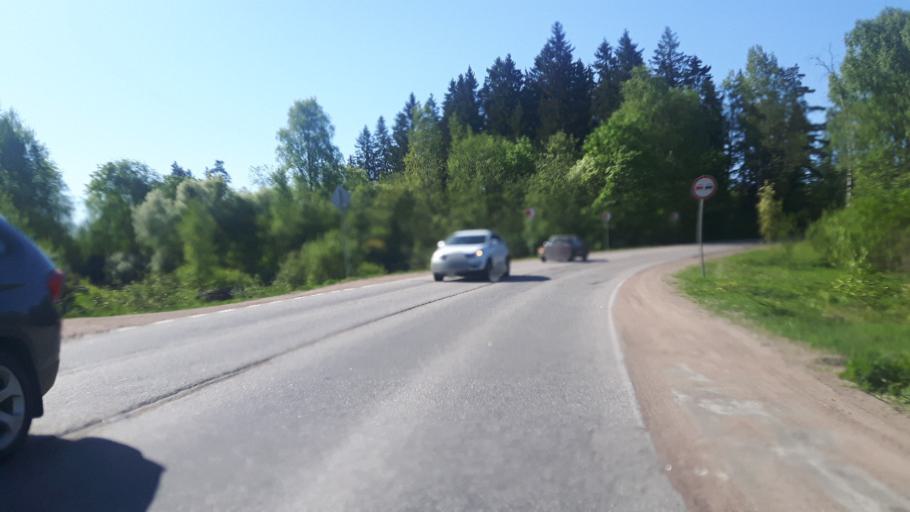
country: RU
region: Leningrad
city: Vyborg
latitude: 60.6481
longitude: 28.7494
